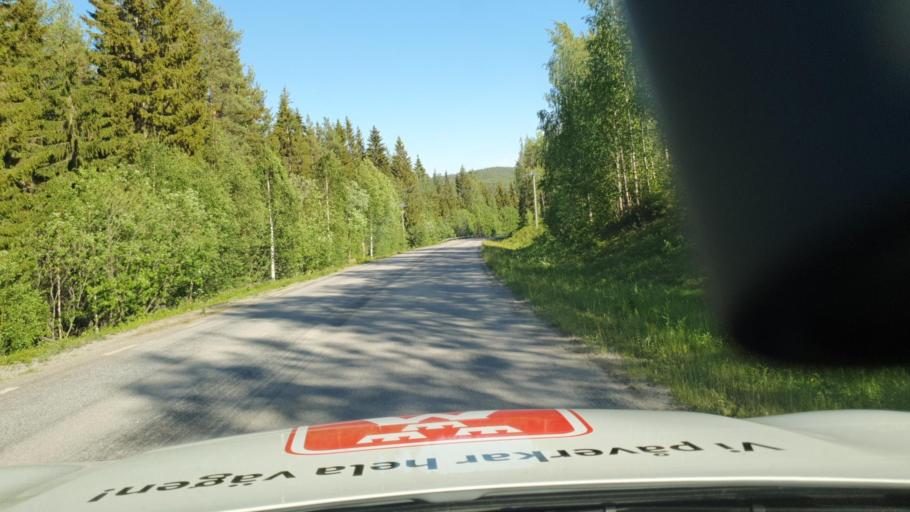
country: SE
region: Vaesterbotten
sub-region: Vannas Kommun
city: Vaennaes
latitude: 63.8918
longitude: 19.7022
